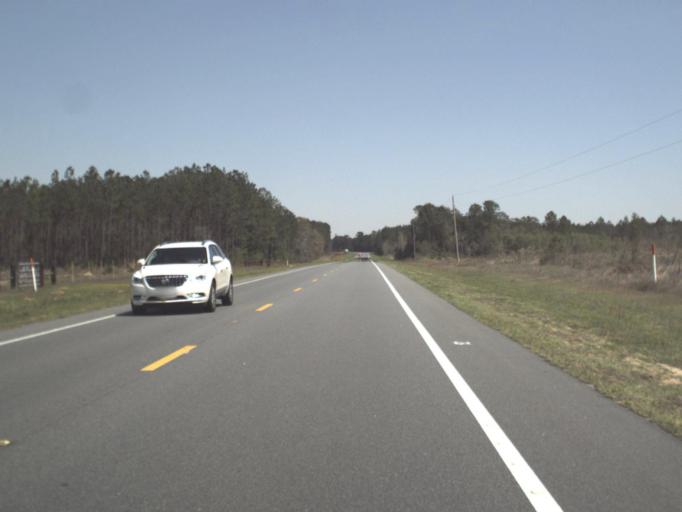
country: US
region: Florida
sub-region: Calhoun County
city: Blountstown
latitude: 30.4336
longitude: -85.2413
